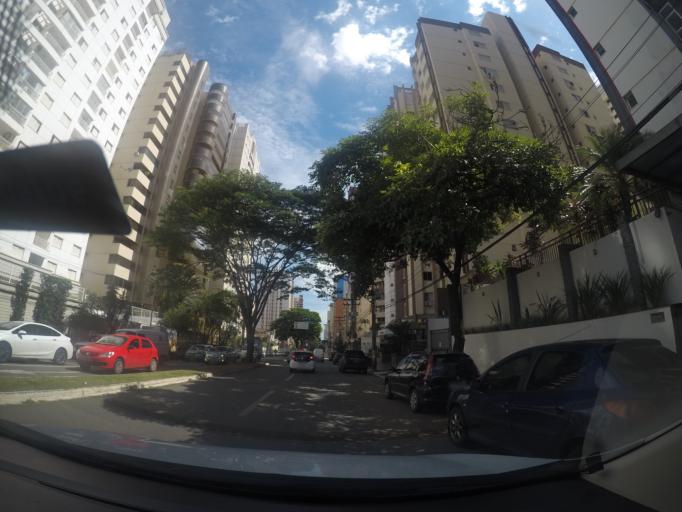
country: BR
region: Goias
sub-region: Goiania
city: Goiania
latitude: -16.7157
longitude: -49.2669
